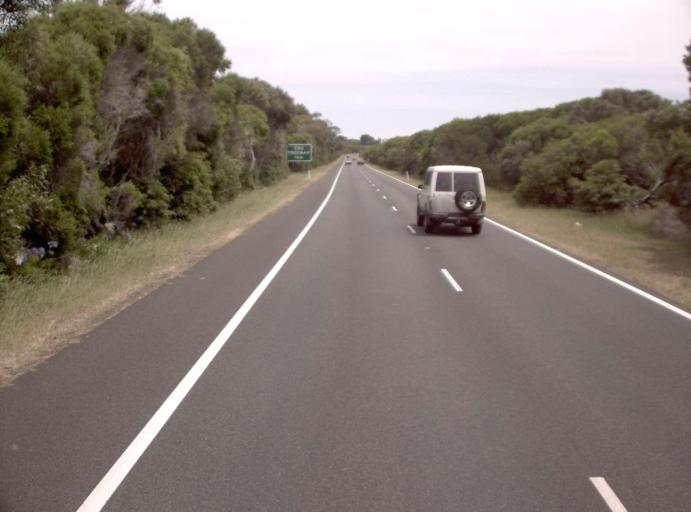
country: AU
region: Victoria
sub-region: Mornington Peninsula
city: McCrae
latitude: -38.3607
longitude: 144.9207
